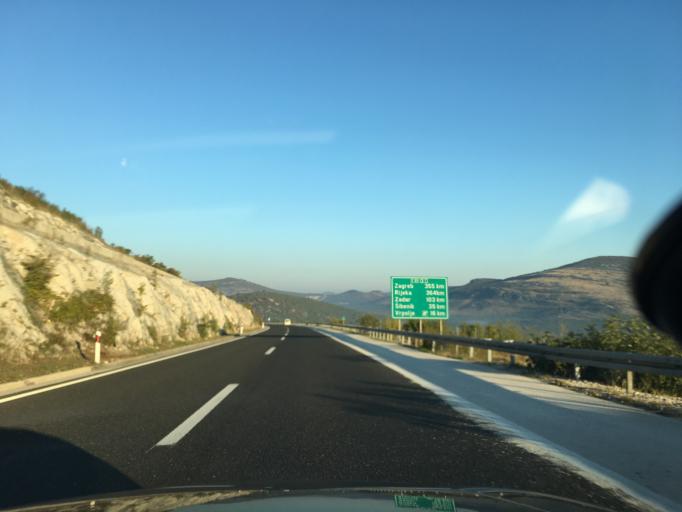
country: HR
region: Splitsko-Dalmatinska
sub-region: Grad Trogir
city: Trogir
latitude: 43.6291
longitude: 16.2320
